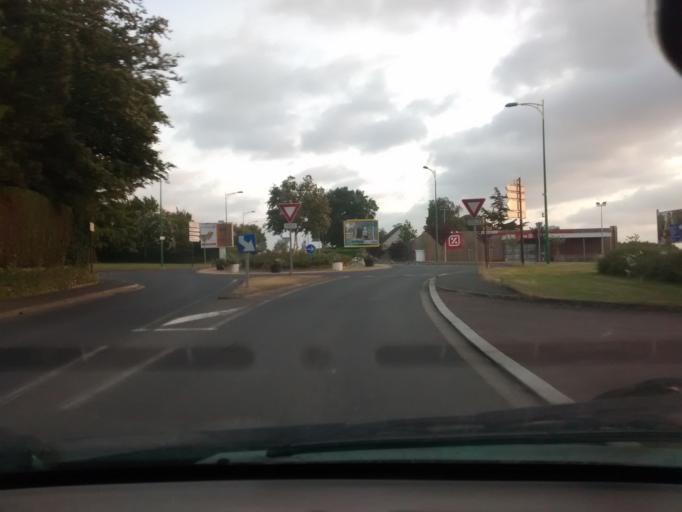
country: FR
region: Lower Normandy
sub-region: Departement de la Manche
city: Agneaux
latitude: 49.1034
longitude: -1.1132
